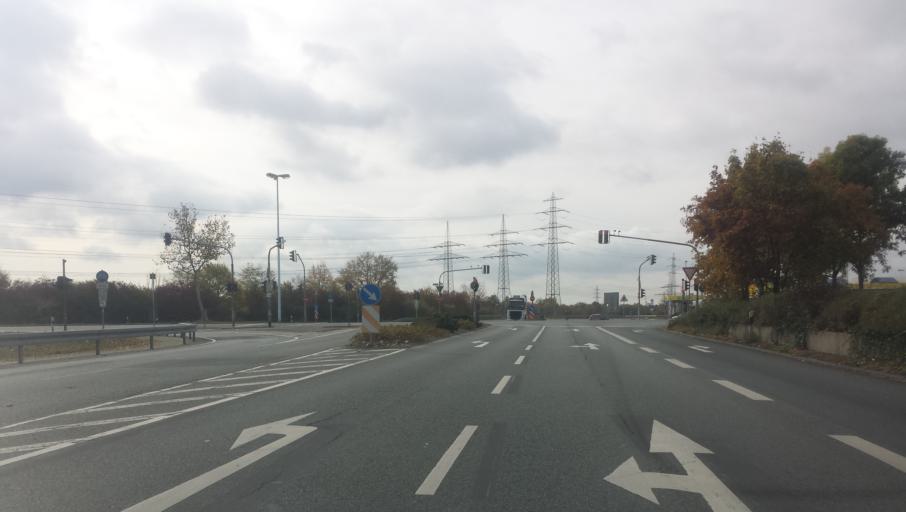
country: DE
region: Hesse
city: Kelsterbach
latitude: 50.0813
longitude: 8.5467
